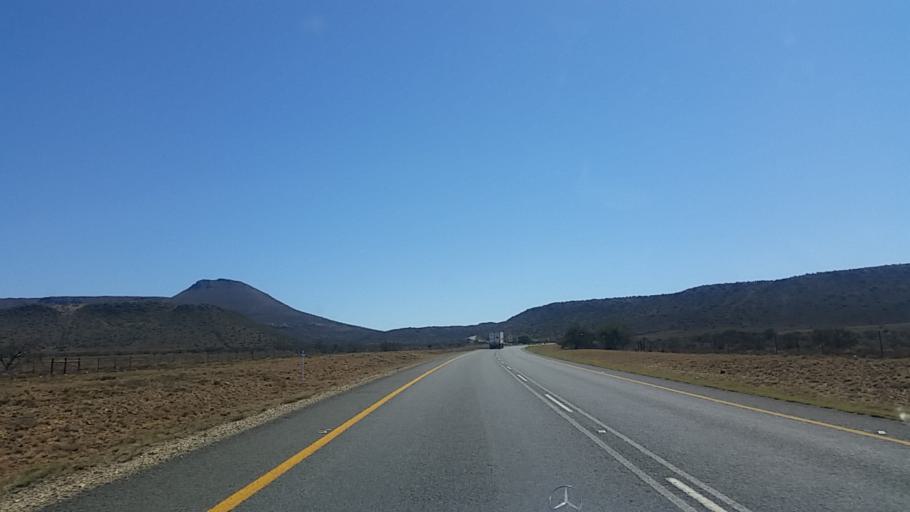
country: ZA
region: Eastern Cape
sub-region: Cacadu District Municipality
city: Graaff-Reinet
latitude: -32.0772
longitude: 24.6027
